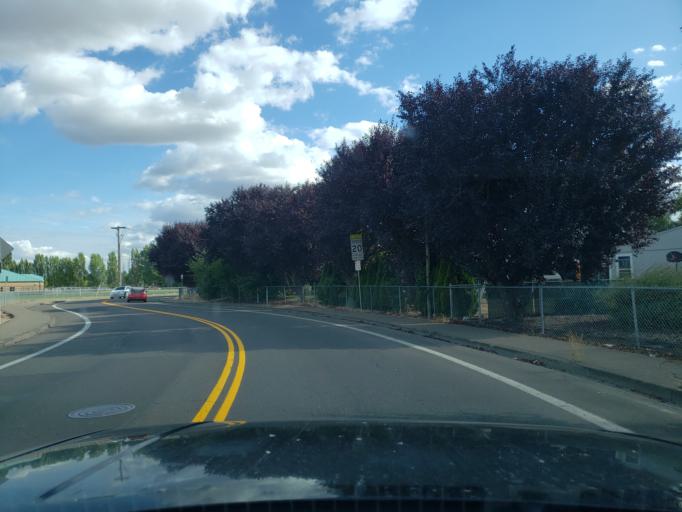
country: US
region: Oregon
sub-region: Yamhill County
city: McMinnville
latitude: 45.2014
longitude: -123.2196
